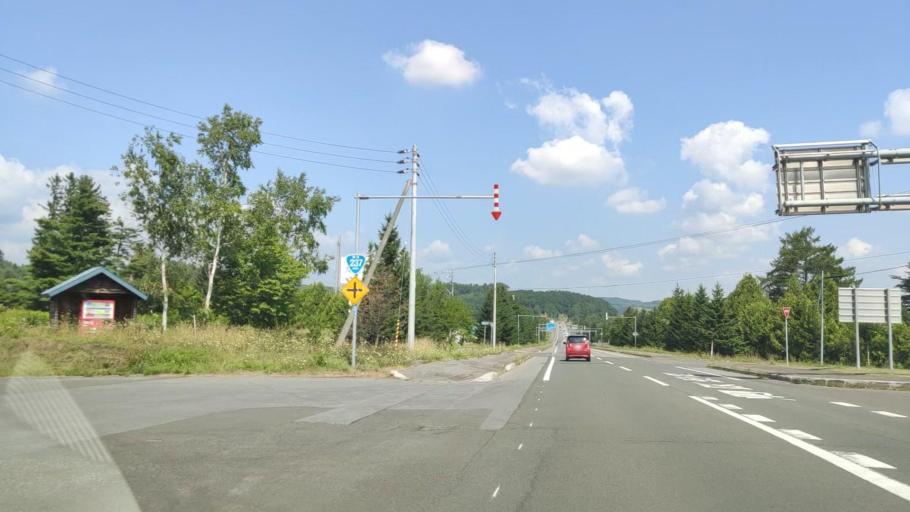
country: JP
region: Hokkaido
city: Shimo-furano
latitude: 43.4629
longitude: 142.4570
